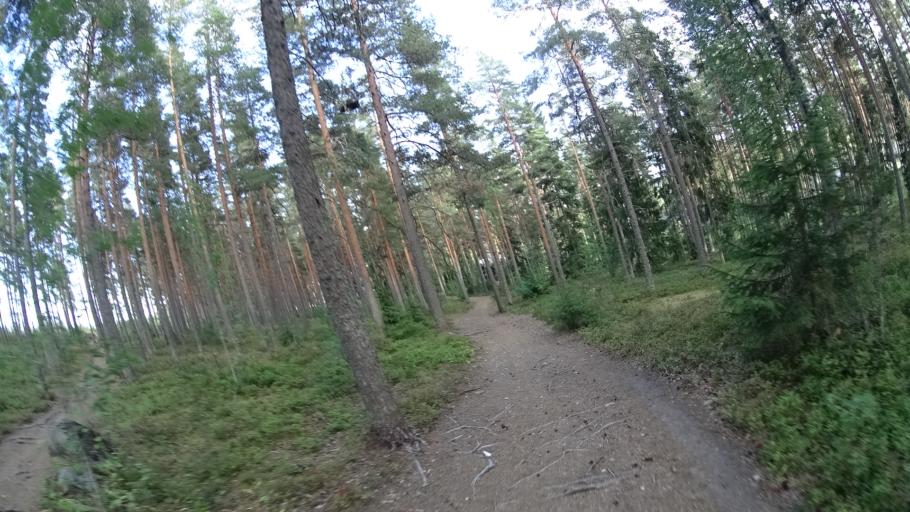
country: FI
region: Uusimaa
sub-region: Helsinki
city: Vihti
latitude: 60.3347
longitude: 24.3053
